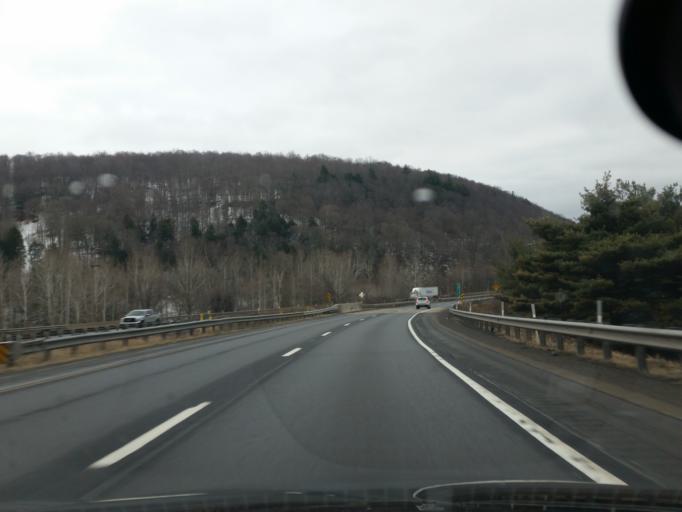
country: US
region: Pennsylvania
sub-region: Wyoming County
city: Factoryville
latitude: 41.7146
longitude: -75.6717
